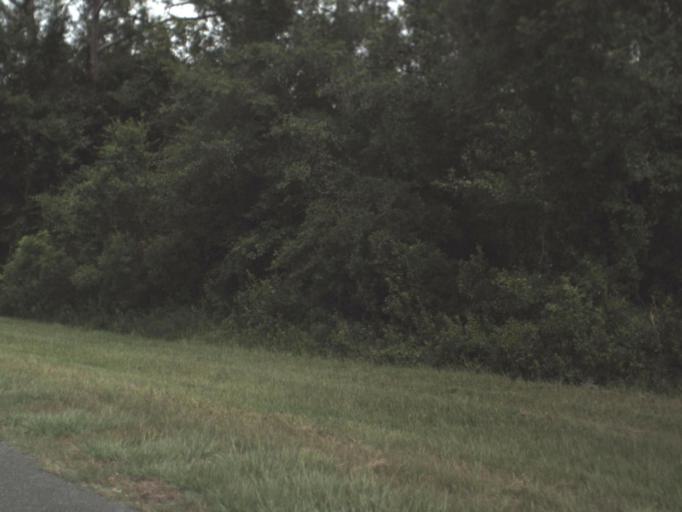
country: US
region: Florida
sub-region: Taylor County
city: Perry
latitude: 30.0978
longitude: -83.4755
